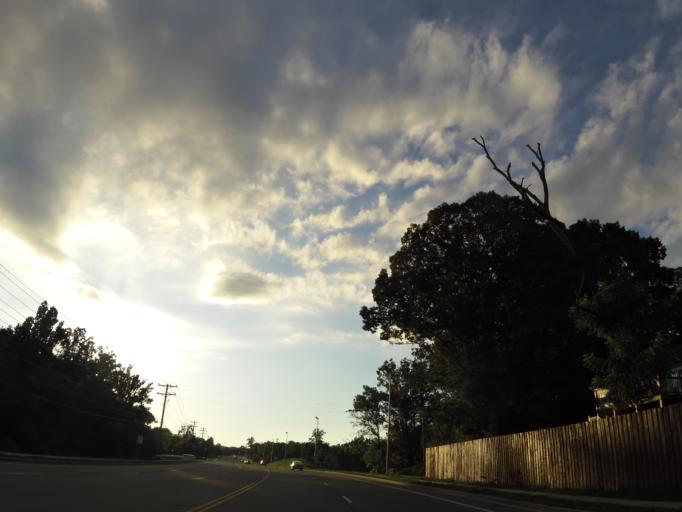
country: US
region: Tennessee
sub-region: Knox County
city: Farragut
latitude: 35.8868
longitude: -84.1644
